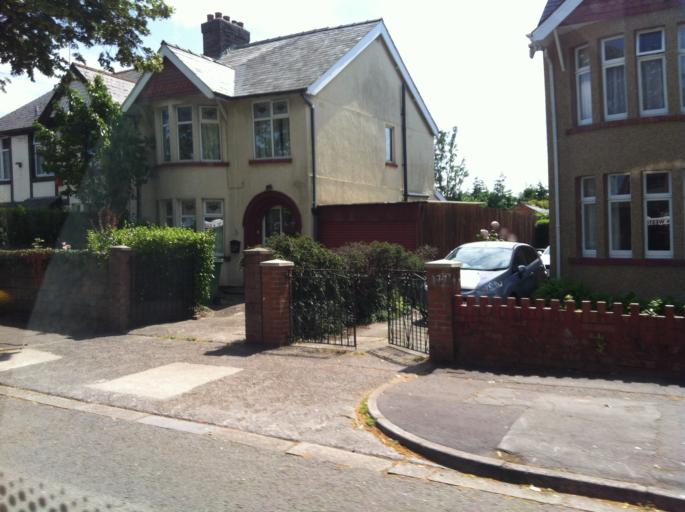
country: GB
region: Wales
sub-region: Cardiff
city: Radyr
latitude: 51.4899
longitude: -3.2423
